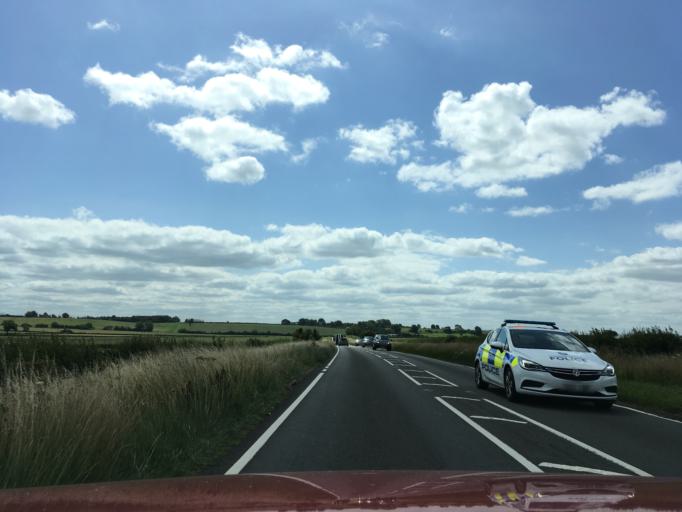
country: GB
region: England
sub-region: Buckinghamshire
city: Winslow
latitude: 51.9066
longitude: -0.8365
